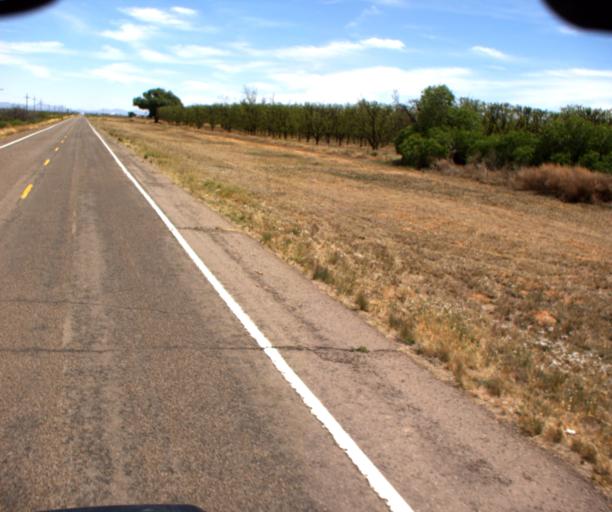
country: US
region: Arizona
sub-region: Cochise County
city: Willcox
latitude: 32.3240
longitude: -109.4689
